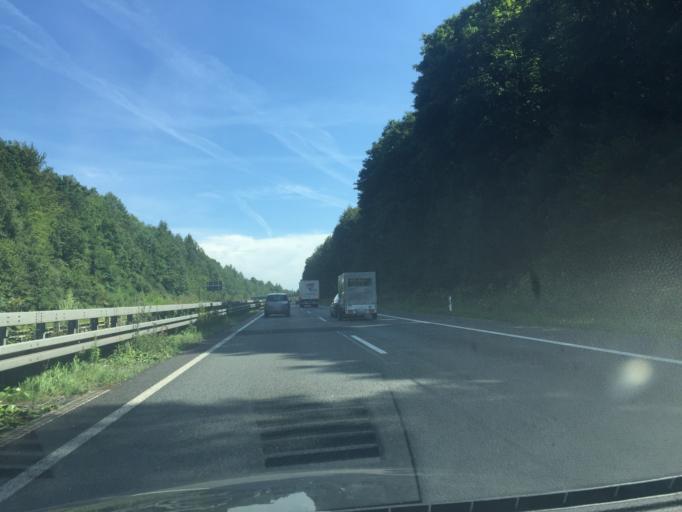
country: DE
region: North Rhine-Westphalia
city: Meinerzhagen
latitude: 51.0950
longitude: 7.6808
